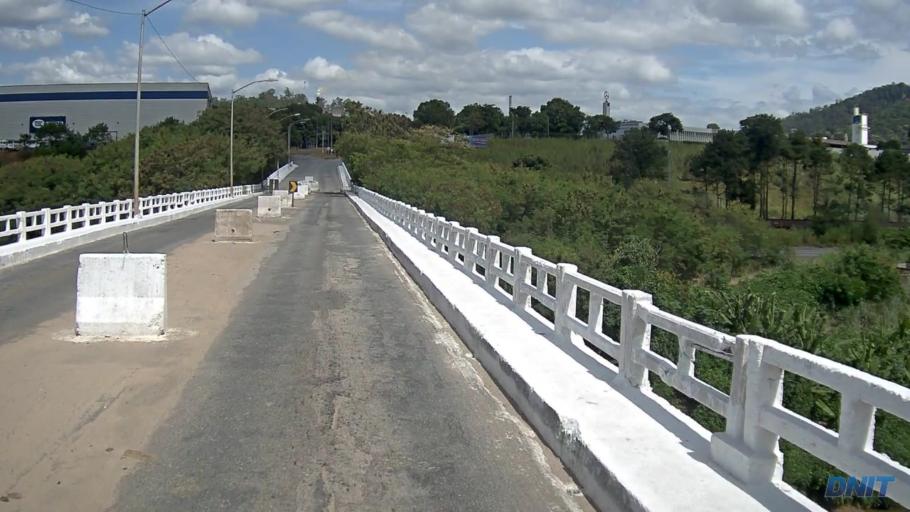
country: BR
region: Minas Gerais
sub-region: Coronel Fabriciano
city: Coronel Fabriciano
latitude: -19.5245
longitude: -42.6401
